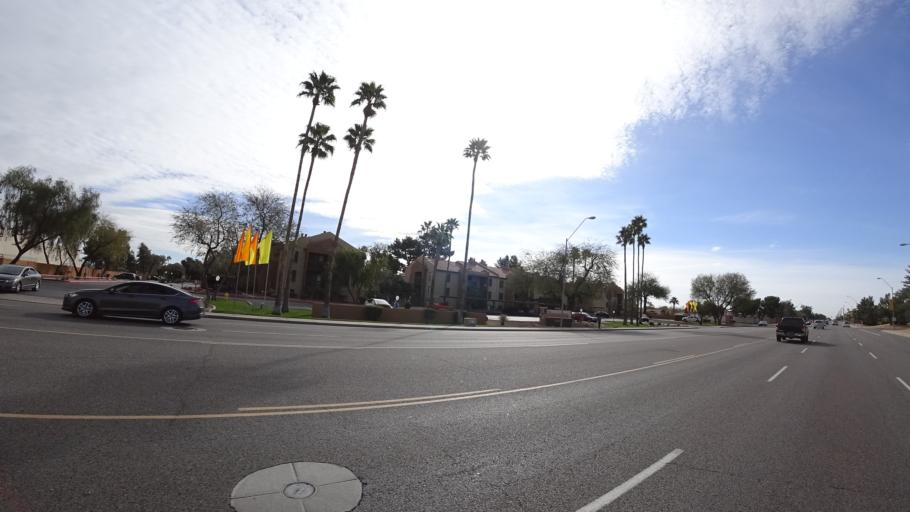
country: US
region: Arizona
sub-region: Maricopa County
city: Glendale
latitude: 33.6084
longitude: -112.1513
